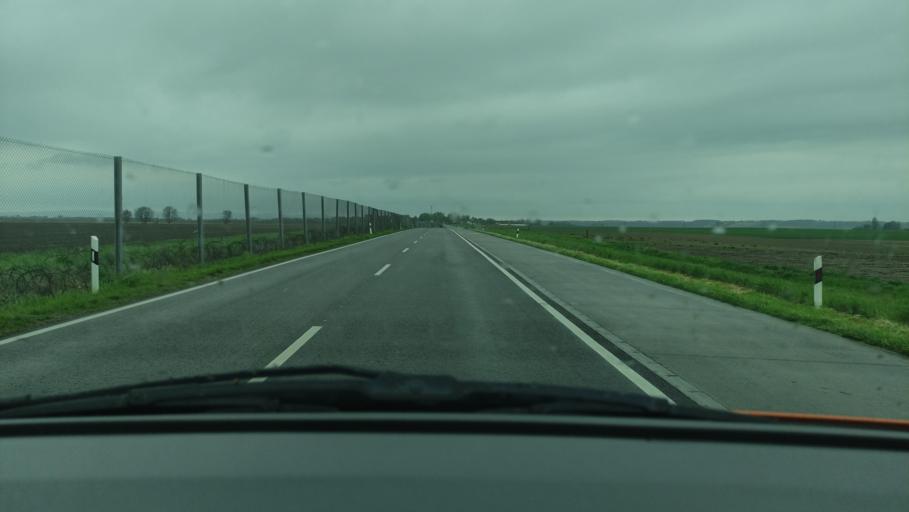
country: HU
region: Baranya
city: Mohacs
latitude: 45.9133
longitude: 18.6596
